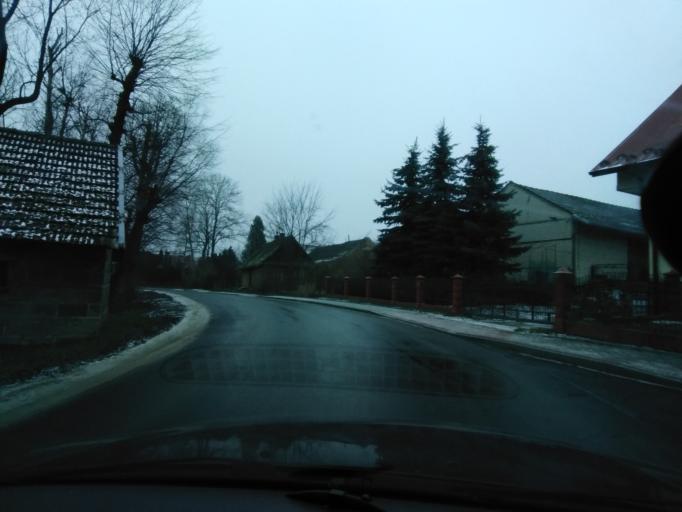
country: PL
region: Subcarpathian Voivodeship
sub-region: Powiat przeworski
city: Gac
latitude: 50.0247
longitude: 22.3920
